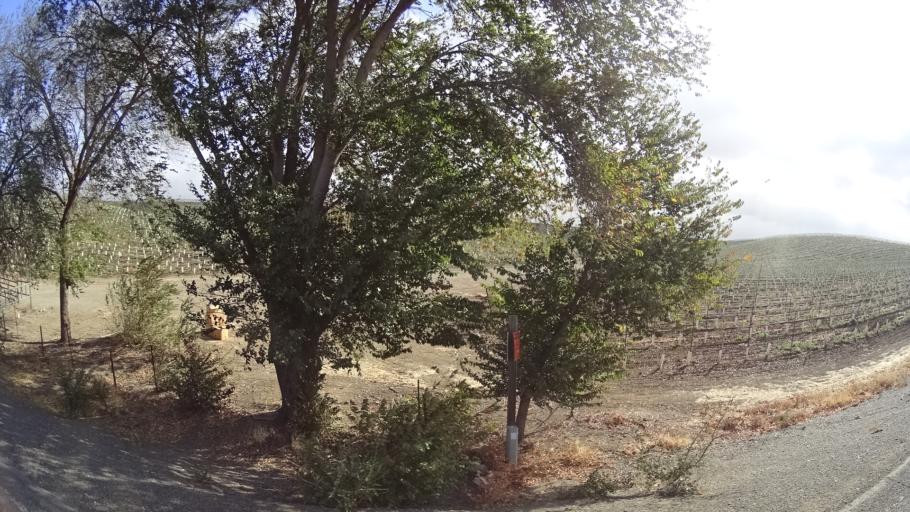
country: US
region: California
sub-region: Yolo County
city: Dunnigan
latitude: 38.7972
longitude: -122.0074
